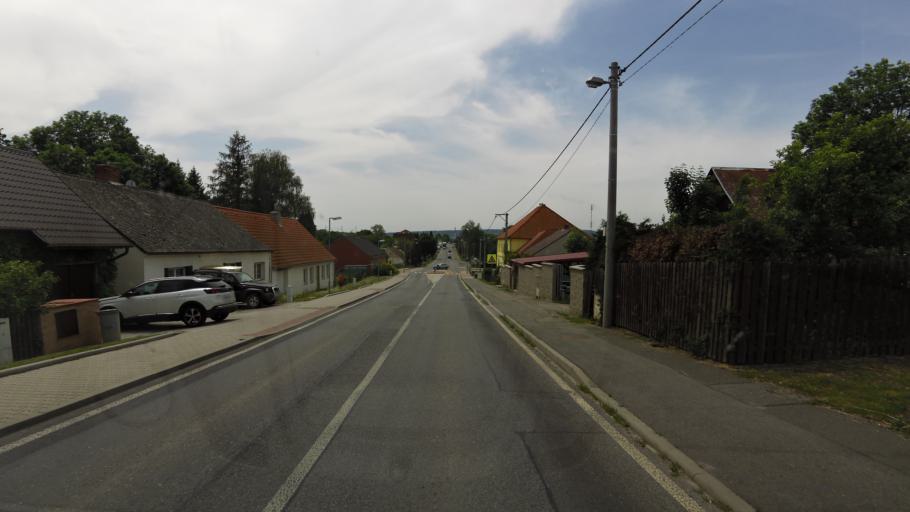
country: CZ
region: Plzensky
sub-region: Okres Rokycany
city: Rokycany
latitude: 49.7482
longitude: 13.6255
